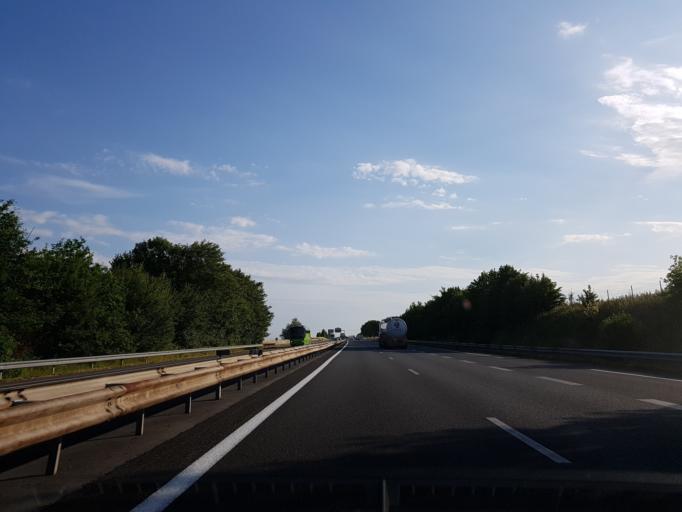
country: FR
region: Nord-Pas-de-Calais
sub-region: Departement du Pas-de-Calais
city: Bourlon
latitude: 50.1427
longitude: 3.1244
